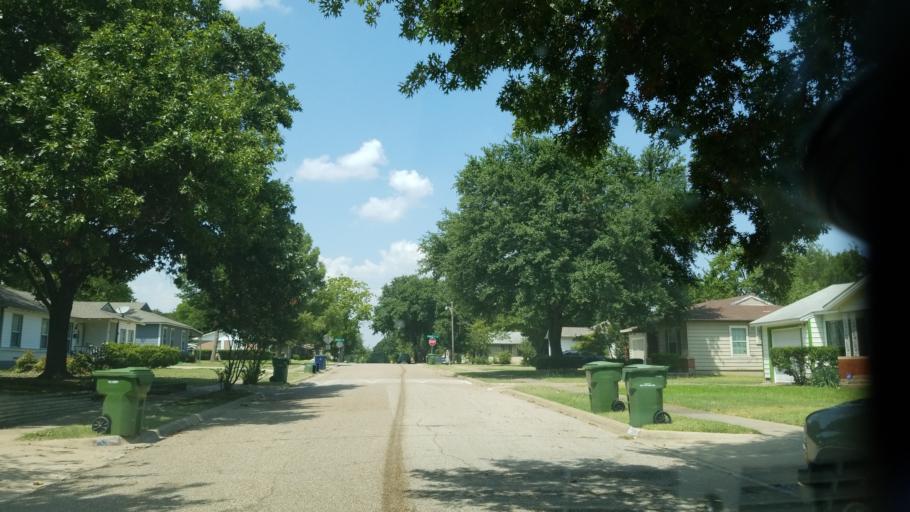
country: US
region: Texas
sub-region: Dallas County
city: Garland
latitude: 32.9252
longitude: -96.6434
